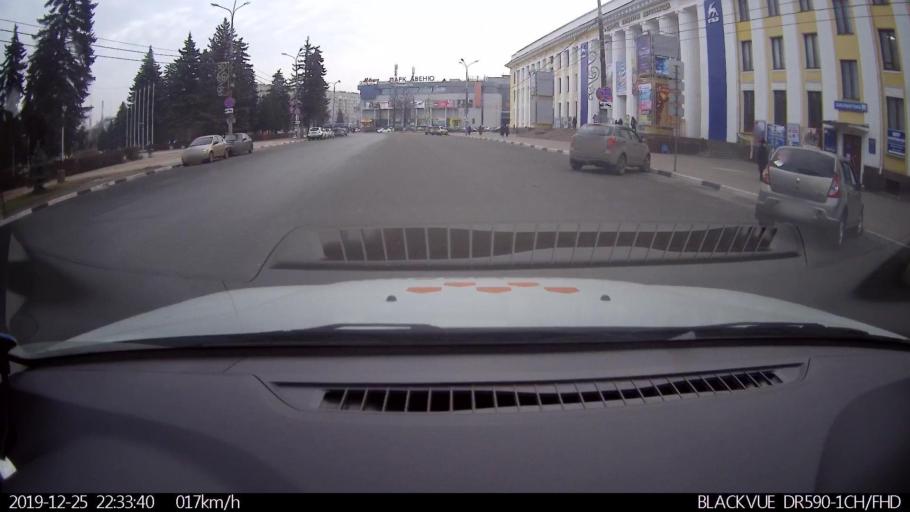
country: RU
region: Nizjnij Novgorod
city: Gorbatovka
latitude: 56.2407
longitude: 43.8612
